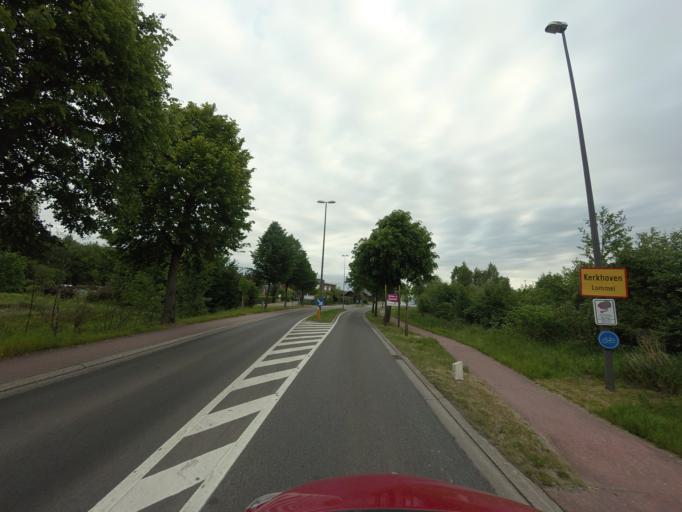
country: BE
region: Flanders
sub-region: Provincie Limburg
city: Leopoldsburg
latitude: 51.1586
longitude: 5.2613
